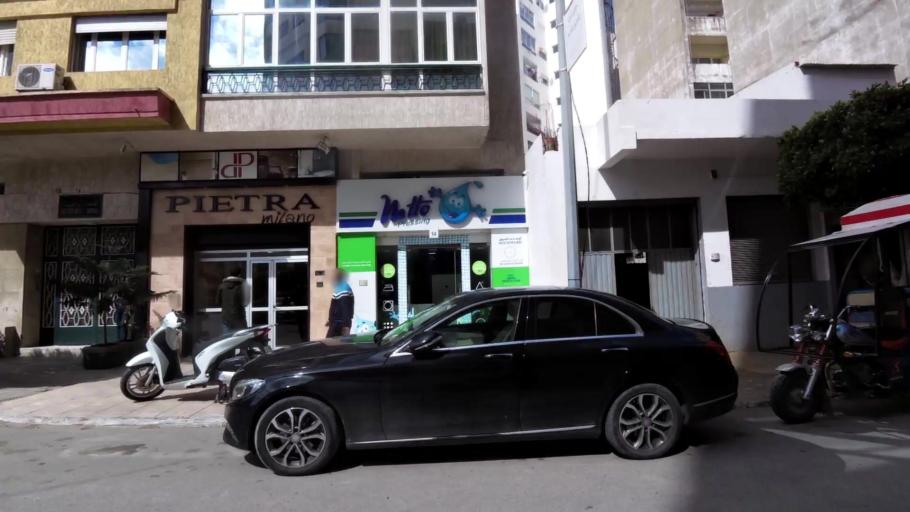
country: MA
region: Tanger-Tetouan
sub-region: Tanger-Assilah
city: Tangier
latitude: 35.7695
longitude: -5.8097
